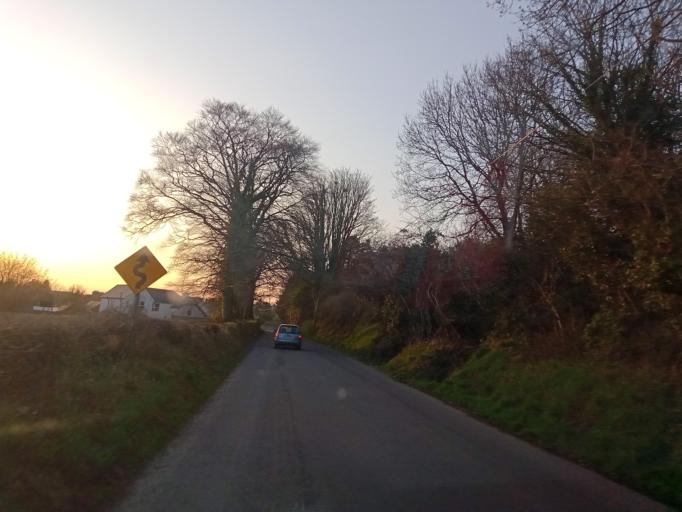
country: IE
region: Leinster
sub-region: Laois
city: Abbeyleix
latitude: 52.8651
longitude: -7.2932
